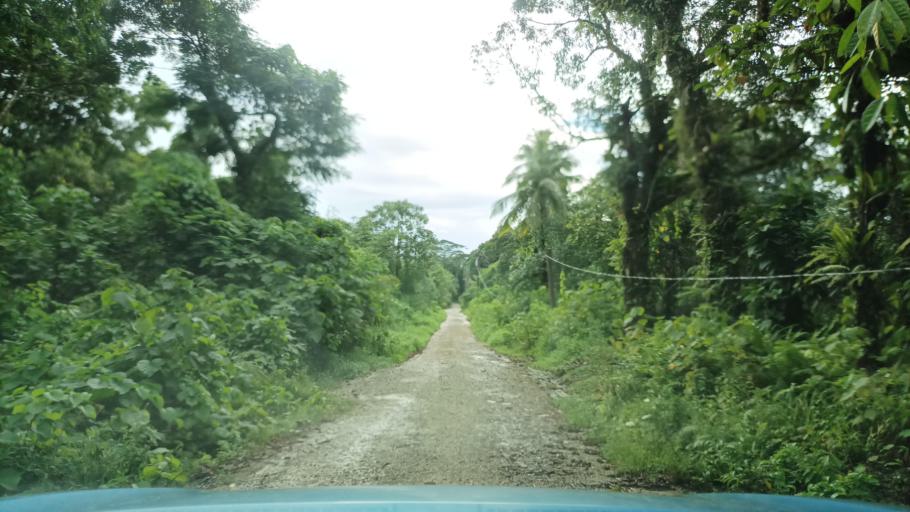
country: FM
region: Pohnpei
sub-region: Sokehs Municipality
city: Palikir - National Government Center
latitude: 6.8810
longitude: 158.1709
